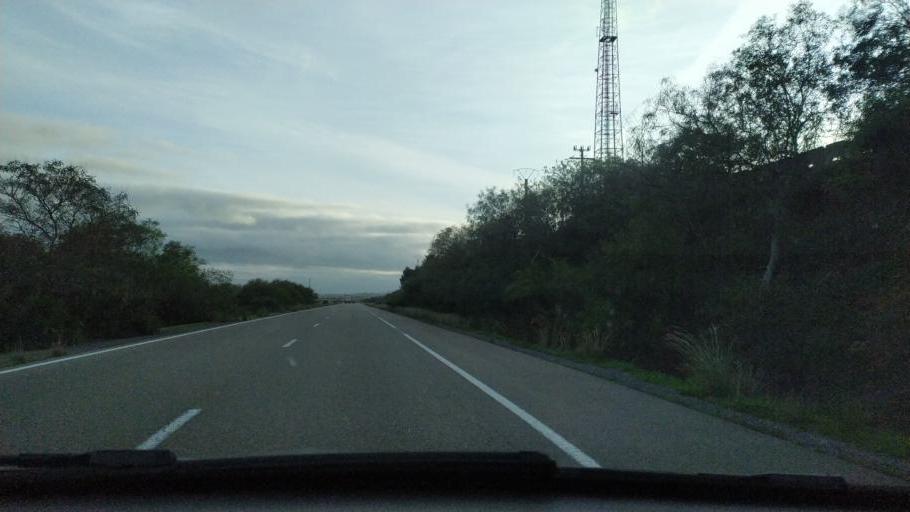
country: MA
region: Gharb-Chrarda-Beni Hssen
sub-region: Kenitra Province
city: Kenitra
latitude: 34.4226
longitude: -6.5204
